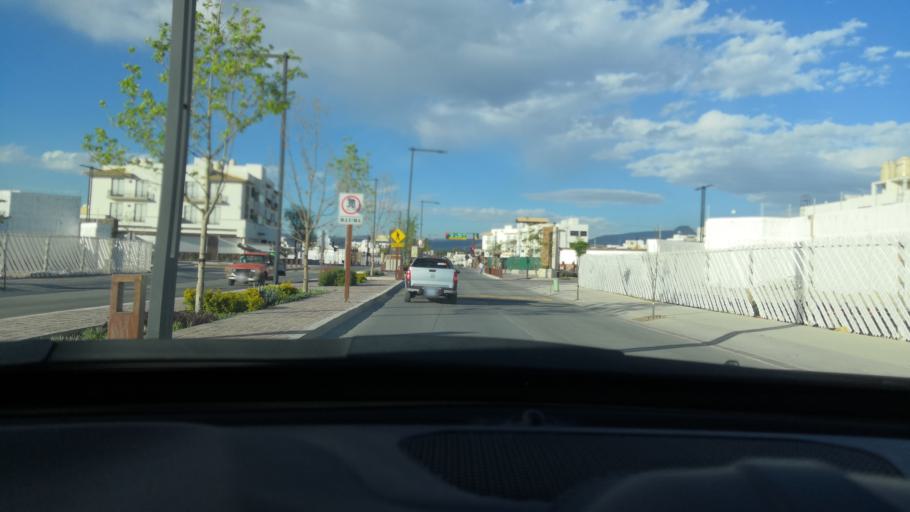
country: MX
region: Guanajuato
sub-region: Leon
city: San Jose de Duran (Los Troncoso)
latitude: 21.0847
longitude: -101.6535
